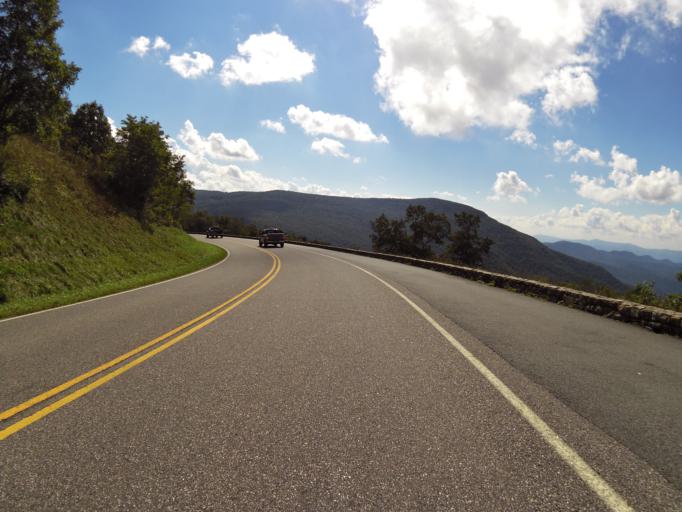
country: US
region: Virginia
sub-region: Page County
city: Stanley
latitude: 38.5477
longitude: -78.4147
